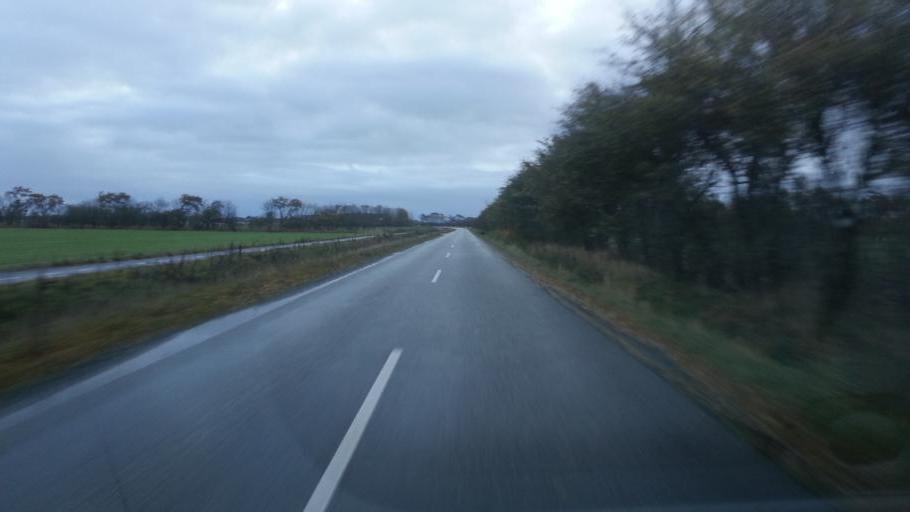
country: DK
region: South Denmark
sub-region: Esbjerg Kommune
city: Tjaereborg
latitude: 55.4589
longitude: 8.6071
